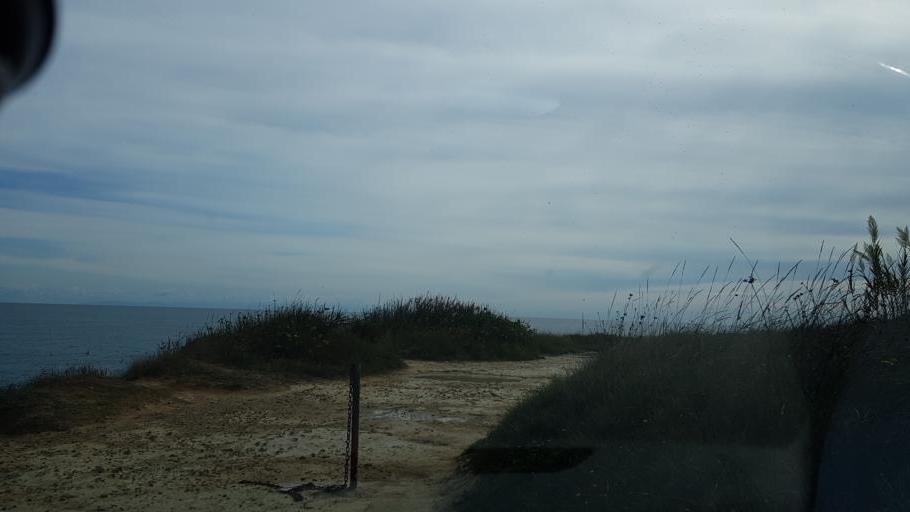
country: IT
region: Apulia
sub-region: Provincia di Lecce
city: Borgagne
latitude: 40.2536
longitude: 18.4457
